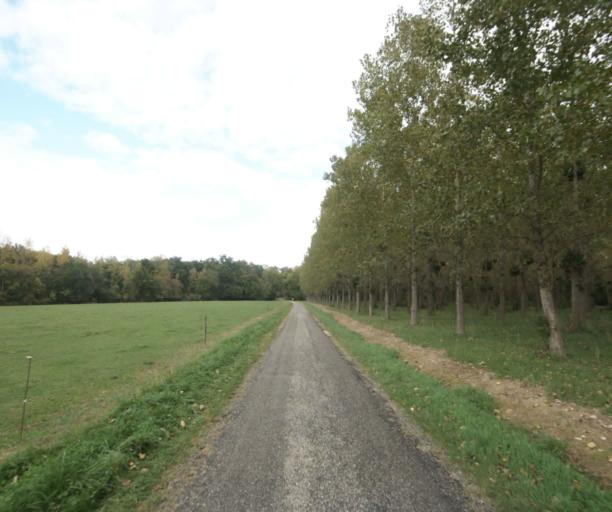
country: FR
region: Midi-Pyrenees
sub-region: Departement du Gers
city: Montreal
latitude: 43.9309
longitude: 0.1449
